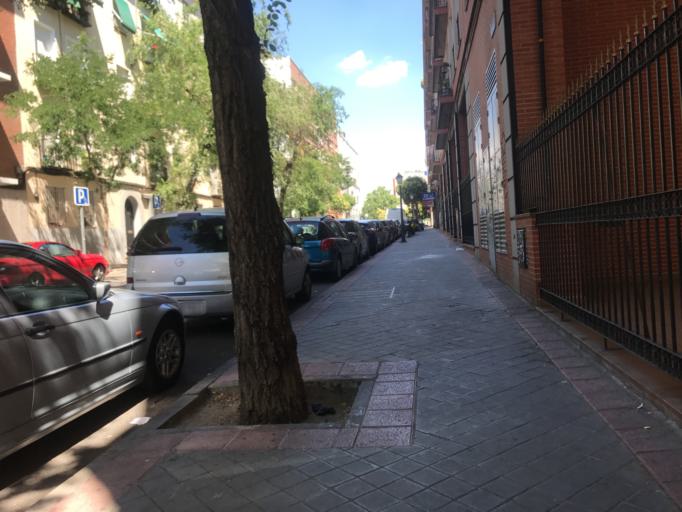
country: ES
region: Madrid
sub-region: Provincia de Madrid
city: Arganzuela
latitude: 40.4016
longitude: -3.6894
